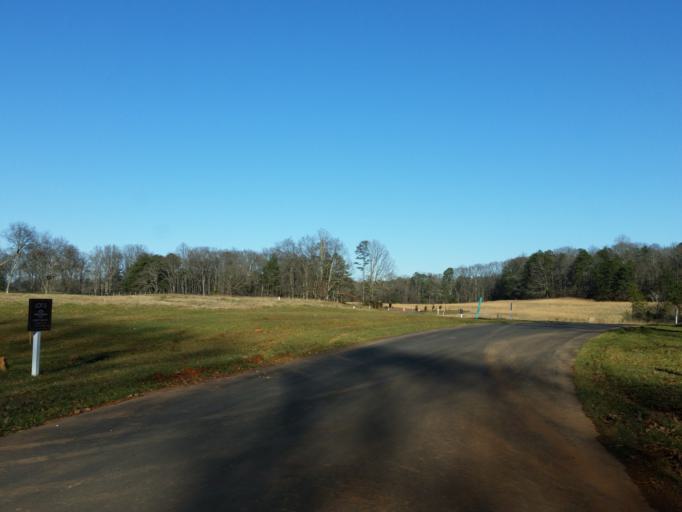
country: US
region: Georgia
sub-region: Cobb County
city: Kennesaw
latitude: 33.9761
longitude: -84.6021
